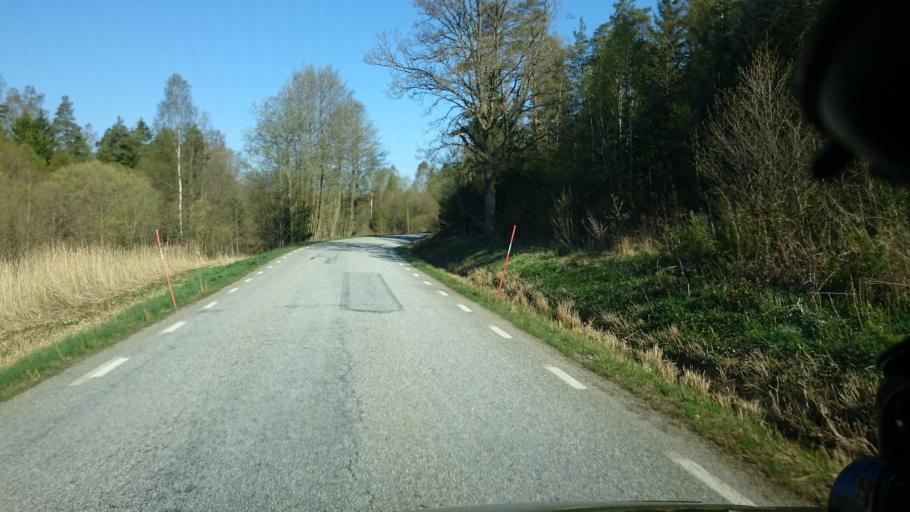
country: SE
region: Vaestra Goetaland
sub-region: Munkedals Kommun
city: Munkedal
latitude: 58.3696
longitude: 11.6919
